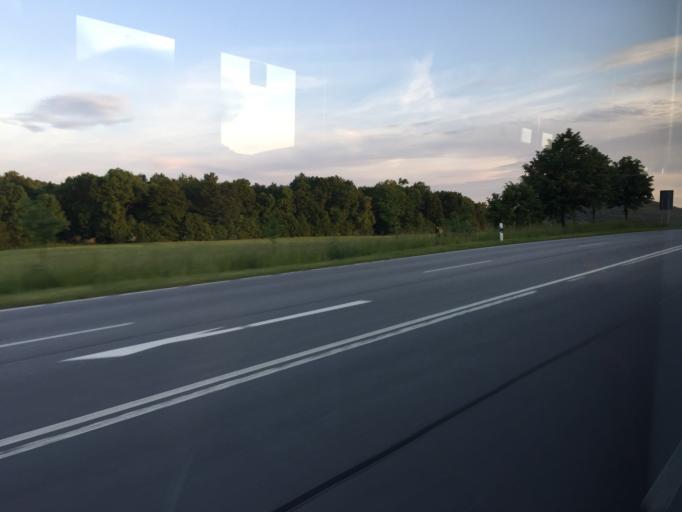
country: DE
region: Saxony
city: Sohland am Rotstein
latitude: 51.1214
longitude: 14.7381
